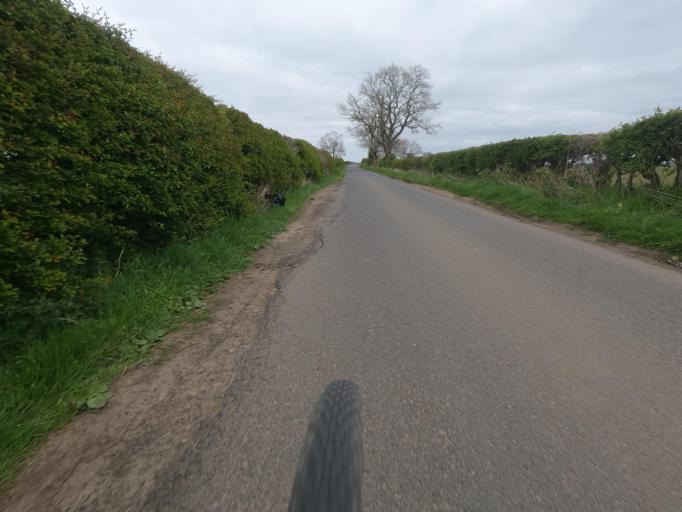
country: GB
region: England
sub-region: Northumberland
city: Darras Hall
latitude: 55.0773
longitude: -1.7911
